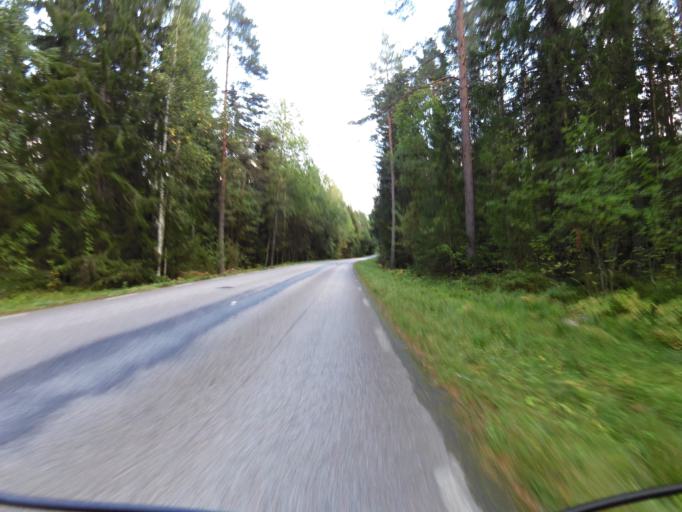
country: SE
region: Gaevleborg
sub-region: Gavle Kommun
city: Valbo
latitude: 60.6651
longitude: 16.9526
